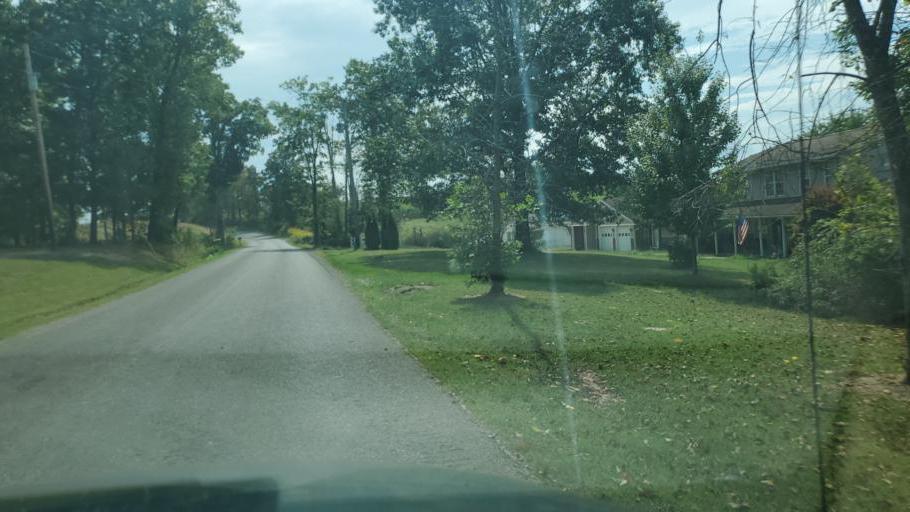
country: US
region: Ohio
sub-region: Muskingum County
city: Frazeysburg
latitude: 39.9760
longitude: -82.1619
